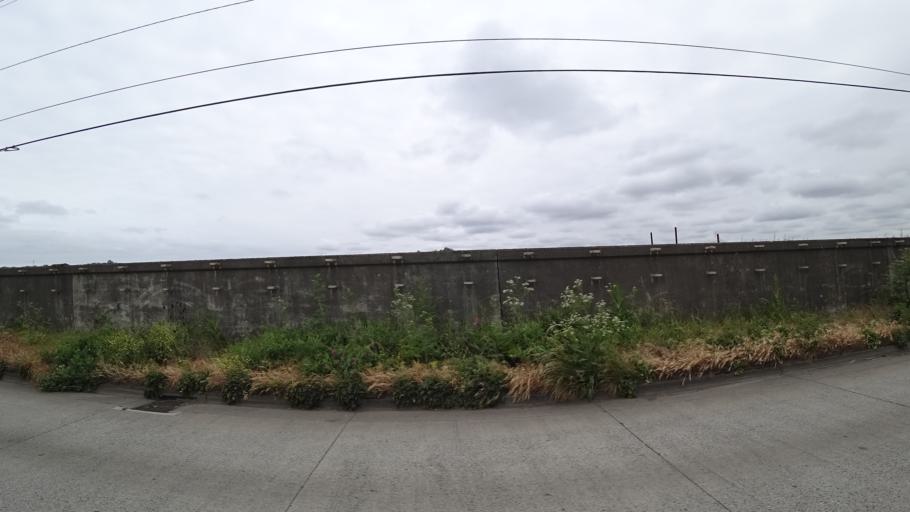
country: US
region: Washington
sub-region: Clark County
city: Vancouver
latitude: 45.6104
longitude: -122.6952
